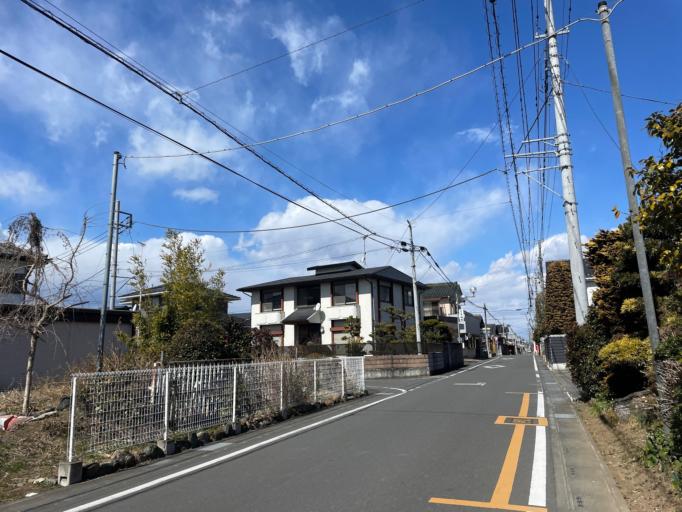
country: JP
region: Saitama
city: Sakado
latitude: 35.9965
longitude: 139.4033
